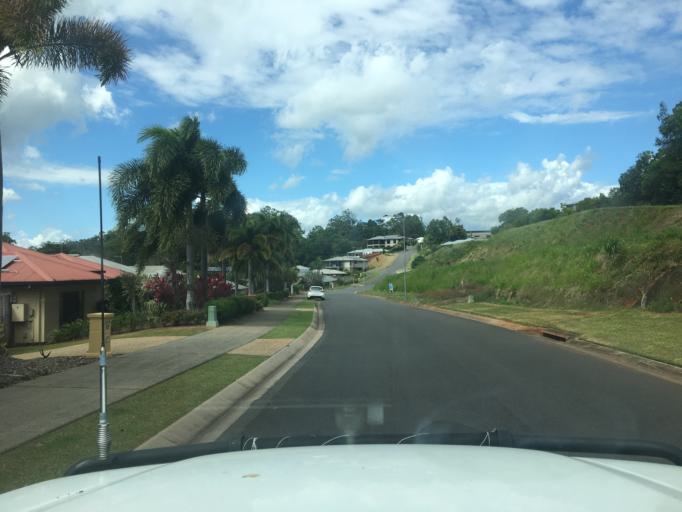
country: AU
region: Queensland
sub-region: Cairns
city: Woree
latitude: -16.9695
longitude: 145.7399
